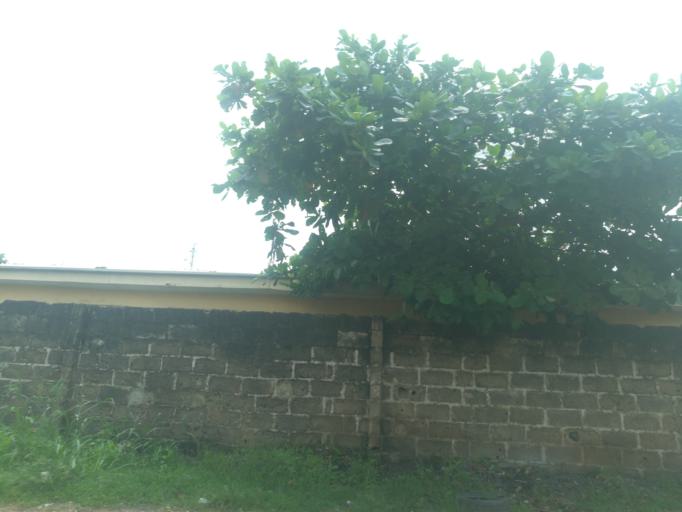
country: NG
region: Oyo
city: Ibadan
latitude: 7.3602
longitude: 3.8676
